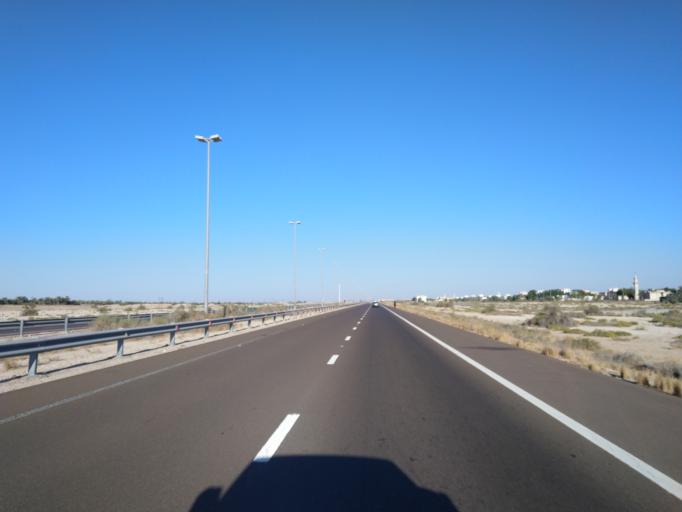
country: OM
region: Al Buraimi
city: Al Buraymi
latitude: 24.5211
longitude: 55.5266
